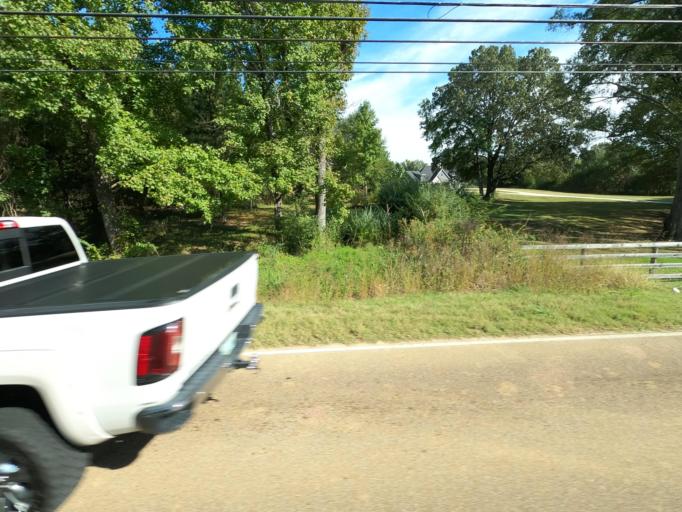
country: US
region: Tennessee
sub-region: Shelby County
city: Arlington
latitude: 35.2378
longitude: -89.6500
